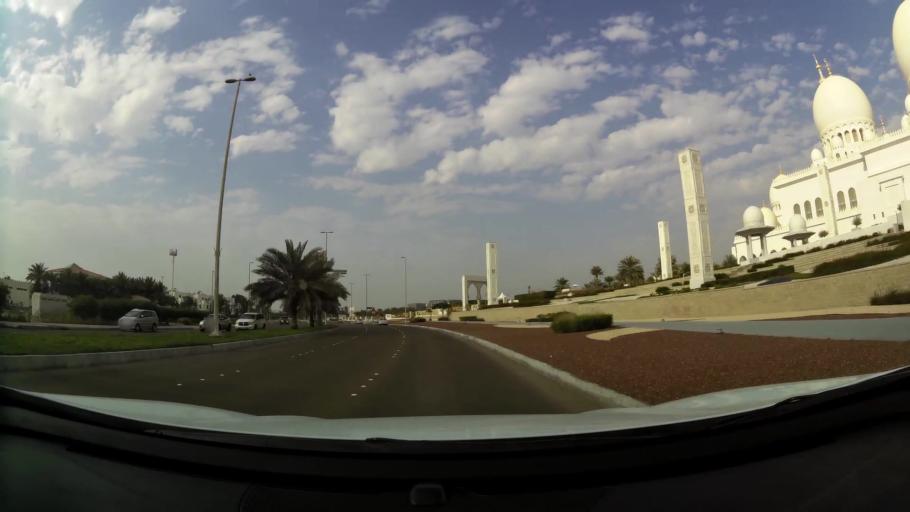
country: AE
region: Abu Dhabi
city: Abu Dhabi
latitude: 24.4126
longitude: 54.4727
